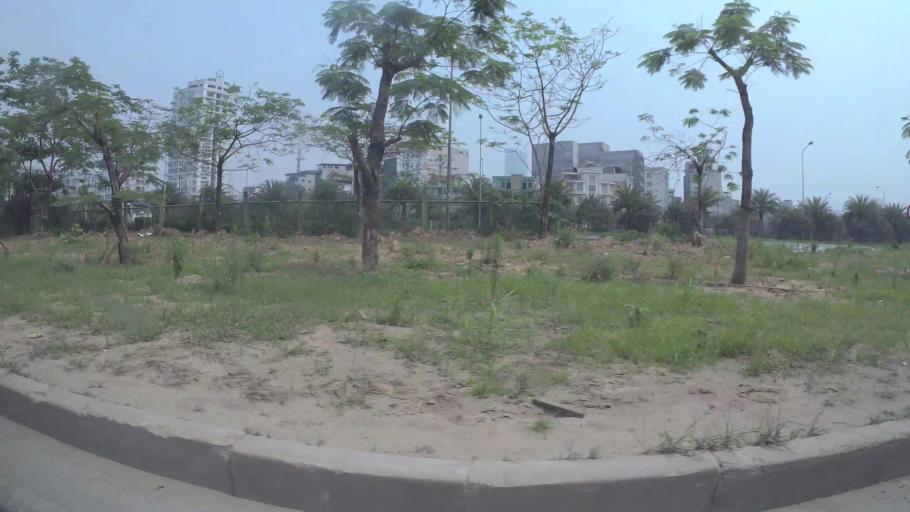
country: VN
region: Ha Noi
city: Thanh Xuan
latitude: 21.0024
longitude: 105.7798
